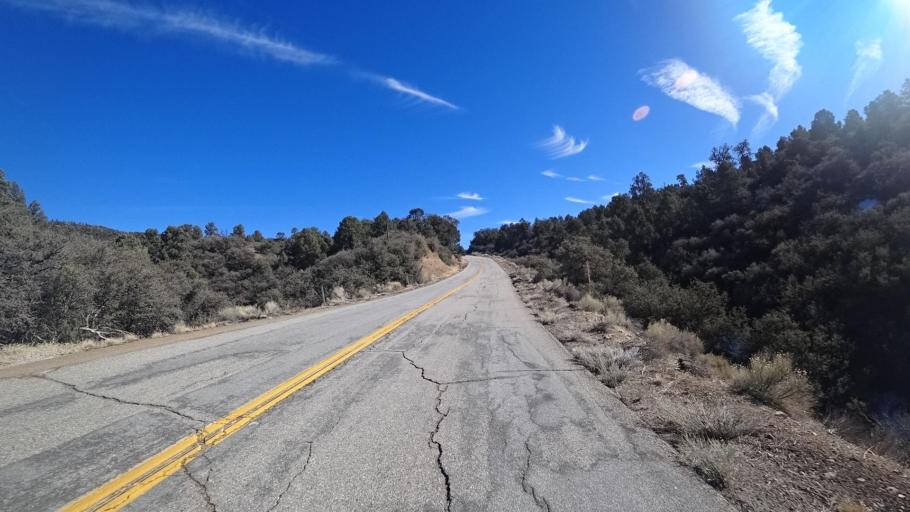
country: US
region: California
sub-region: Kern County
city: Pine Mountain Club
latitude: 34.8653
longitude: -119.2389
